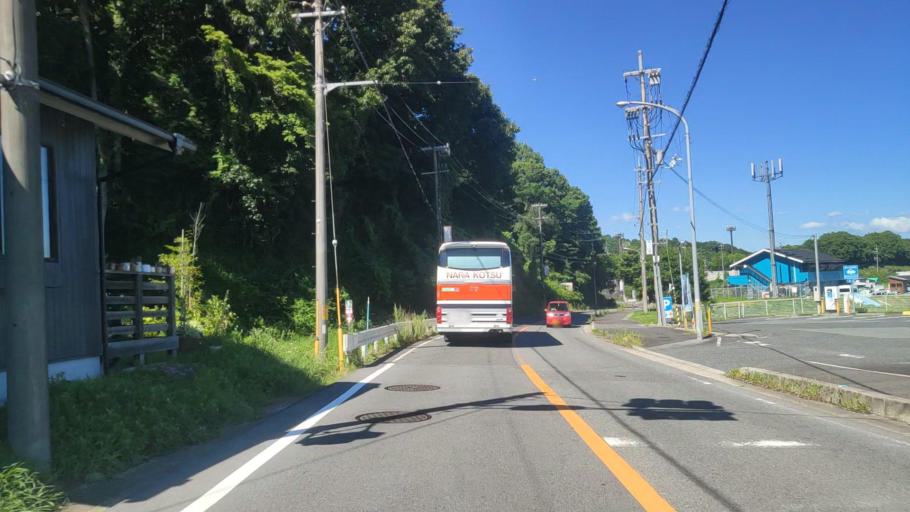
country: JP
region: Nara
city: Haibara-akanedai
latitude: 34.5385
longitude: 135.9534
